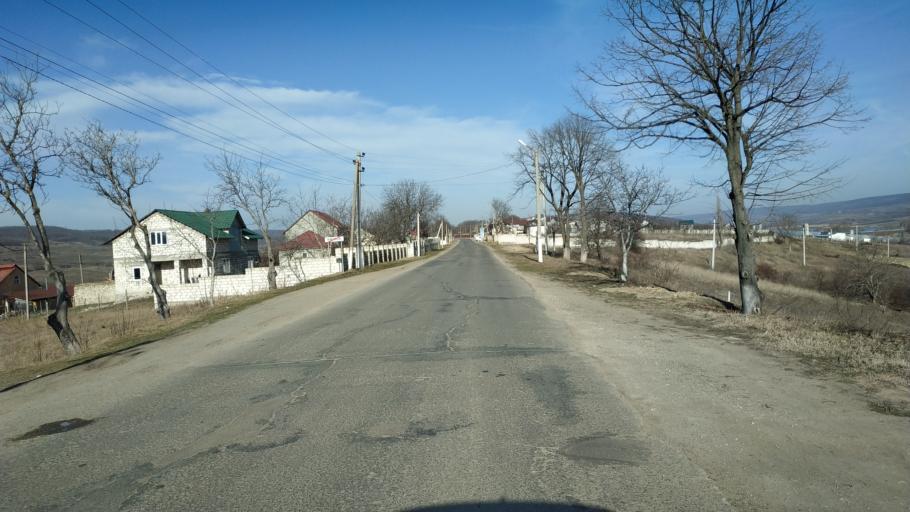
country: MD
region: Chisinau
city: Vatra
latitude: 47.0178
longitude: 28.6523
